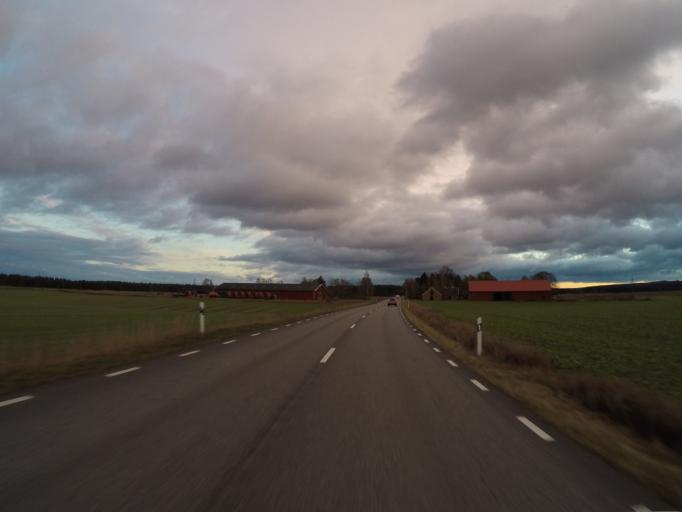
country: SE
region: Skane
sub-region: Kristianstads Kommun
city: Degeberga
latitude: 55.8920
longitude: 14.0850
